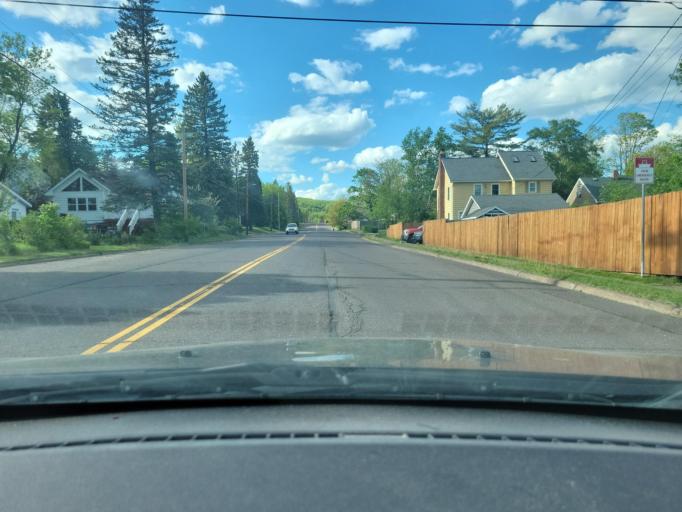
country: US
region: Minnesota
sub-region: Saint Louis County
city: Arnold
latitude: 46.8367
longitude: -92.0293
